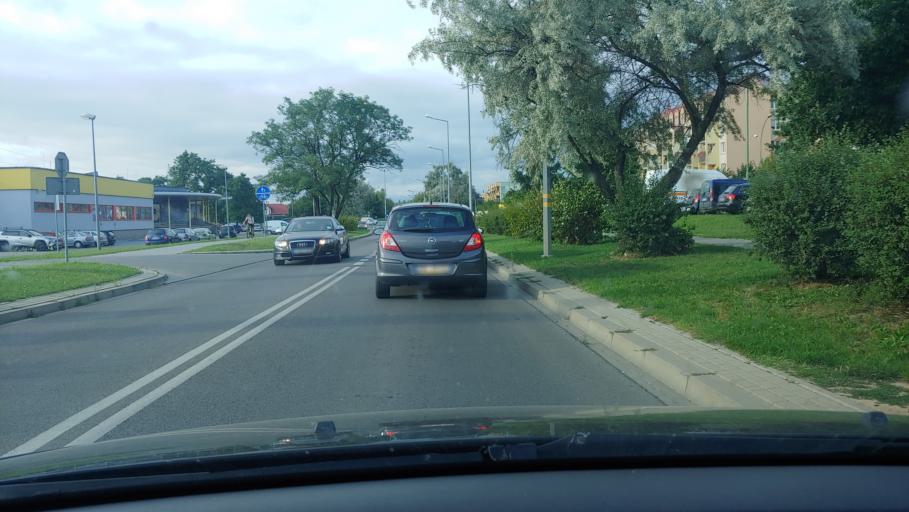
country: PL
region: Subcarpathian Voivodeship
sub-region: Powiat mielecki
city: Mielec
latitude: 50.2888
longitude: 21.4620
